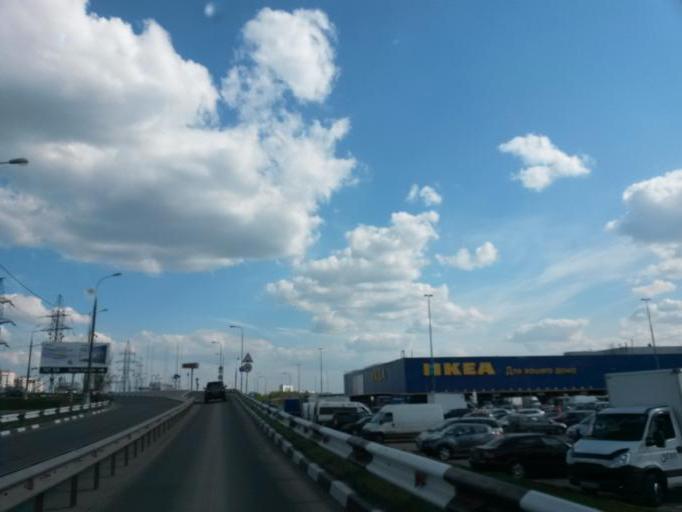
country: RU
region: Moscow
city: Tyoply Stan
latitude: 55.6056
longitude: 37.4958
